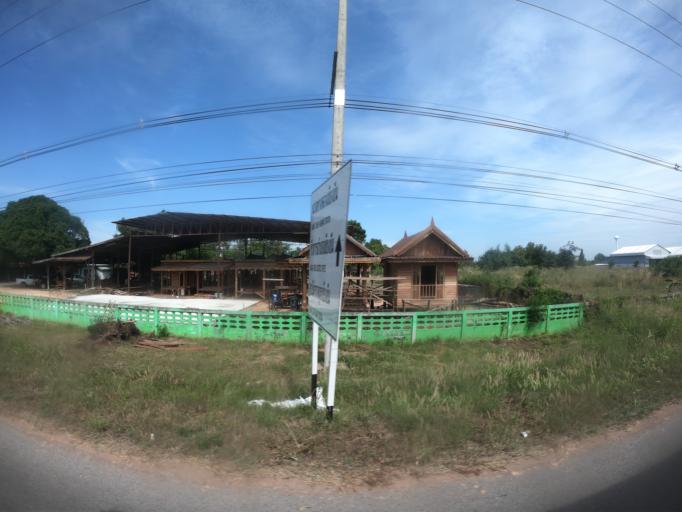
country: TH
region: Maha Sarakham
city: Chiang Yuen
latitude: 16.4445
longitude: 103.0115
